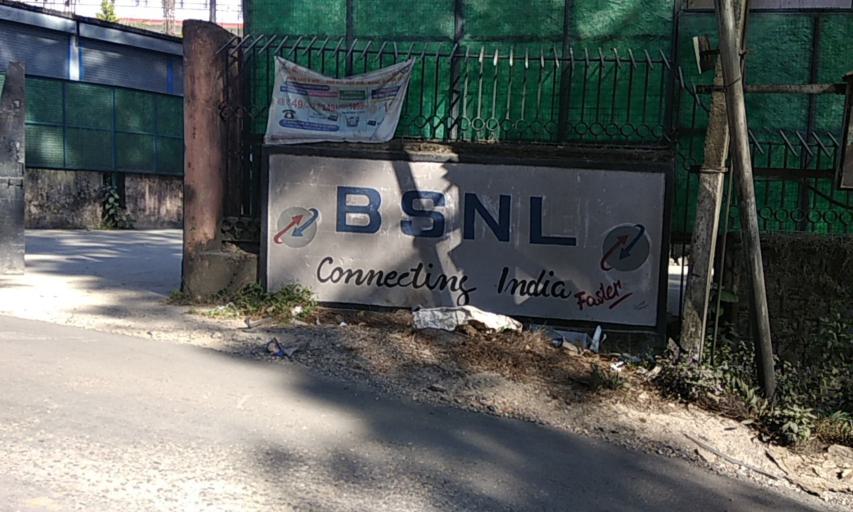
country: IN
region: Himachal Pradesh
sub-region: Kangra
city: Palampur
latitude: 32.1113
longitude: 76.5353
